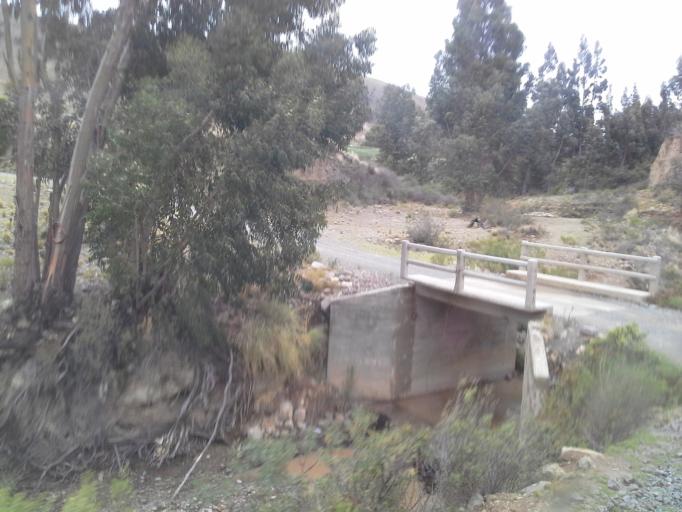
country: BO
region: Cochabamba
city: Colomi
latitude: -17.4166
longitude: -65.8038
